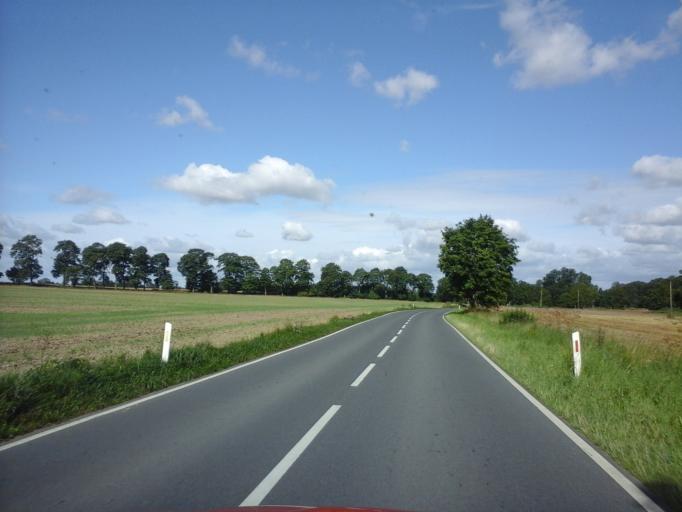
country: PL
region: West Pomeranian Voivodeship
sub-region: Powiat stargardzki
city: Dolice
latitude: 53.2034
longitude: 15.1514
